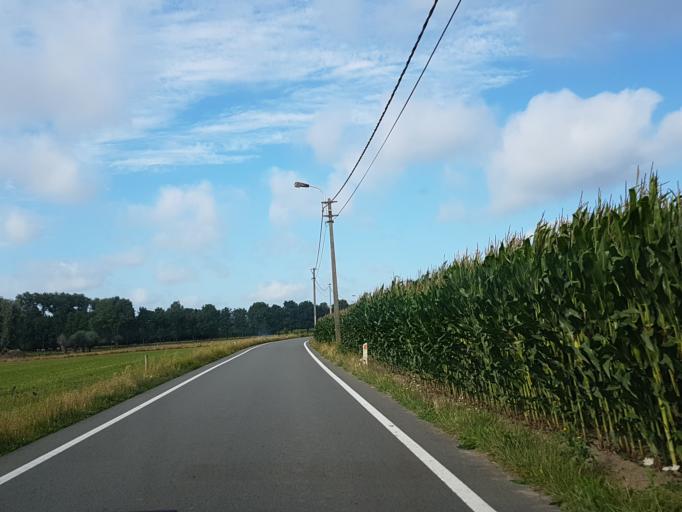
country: BE
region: Flanders
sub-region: Provincie Oost-Vlaanderen
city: Lovendegem
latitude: 51.0727
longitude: 3.5867
